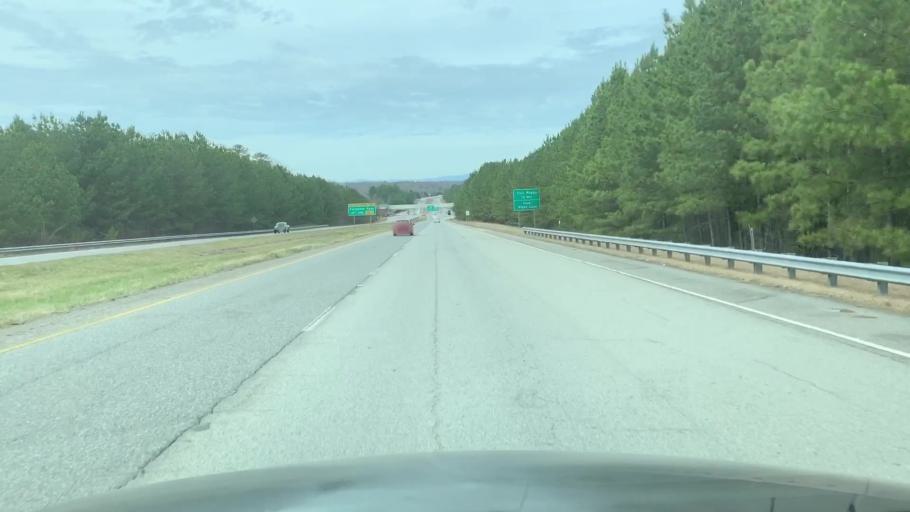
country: US
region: South Carolina
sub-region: Greenville County
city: Golden Grove
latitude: 34.7461
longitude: -82.4409
